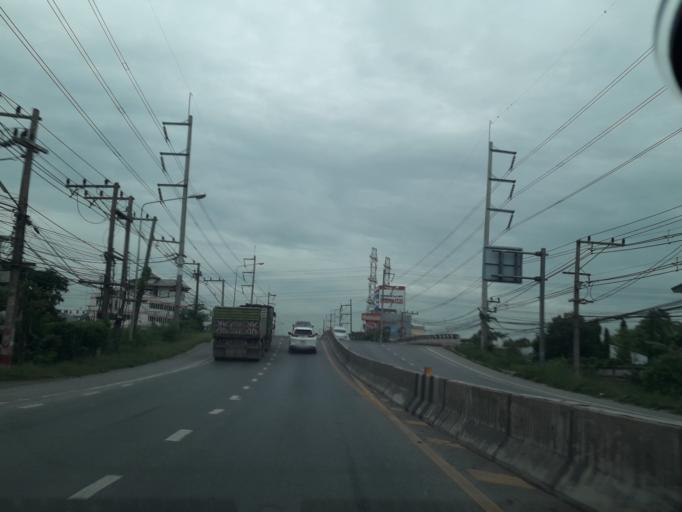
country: TH
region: Pathum Thani
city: Lam Luk Ka
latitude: 13.9435
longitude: 100.7719
